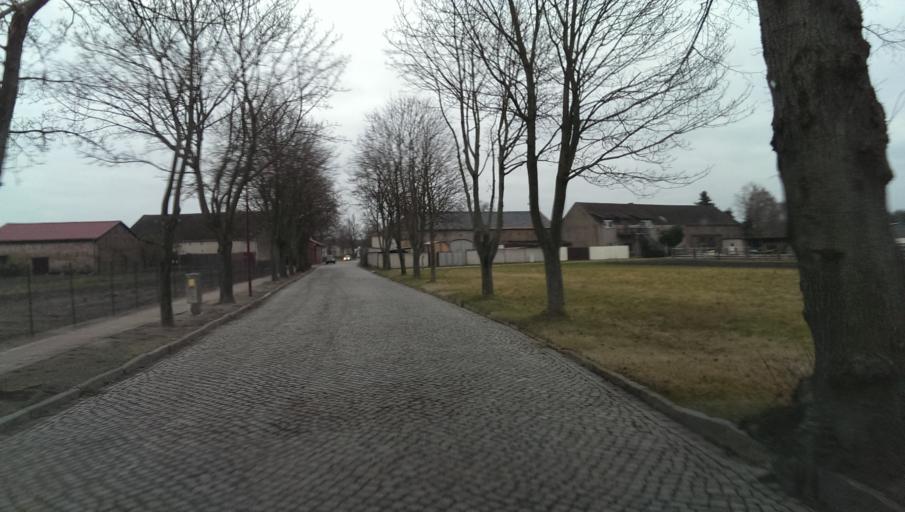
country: DE
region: Brandenburg
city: Mittenwalde
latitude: 52.2252
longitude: 13.5081
